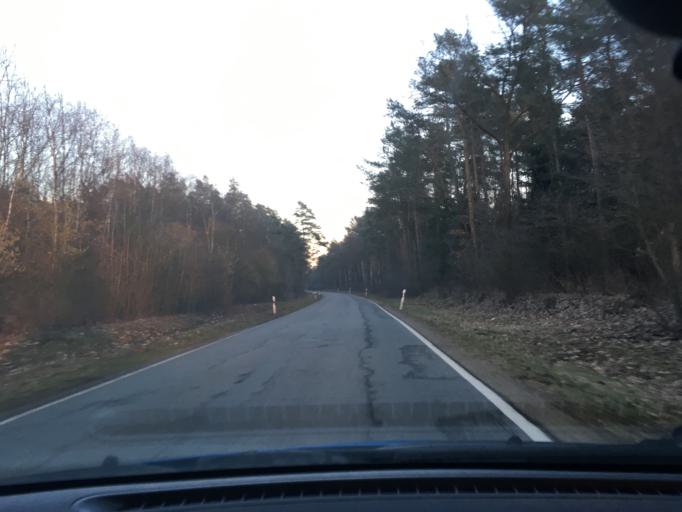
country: DE
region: Schleswig-Holstein
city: Brothen
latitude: 53.4845
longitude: 10.6849
